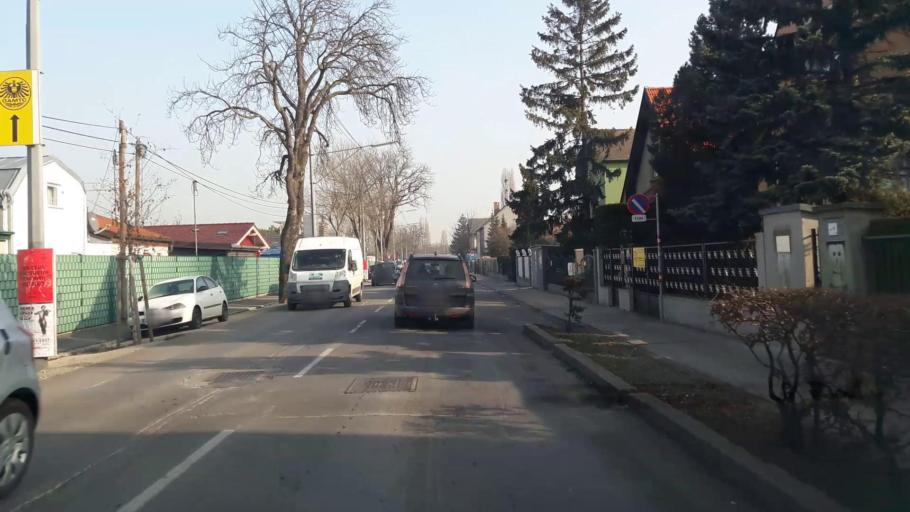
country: AT
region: Lower Austria
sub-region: Politischer Bezirk Modling
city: Vosendorf
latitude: 48.1522
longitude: 16.3245
